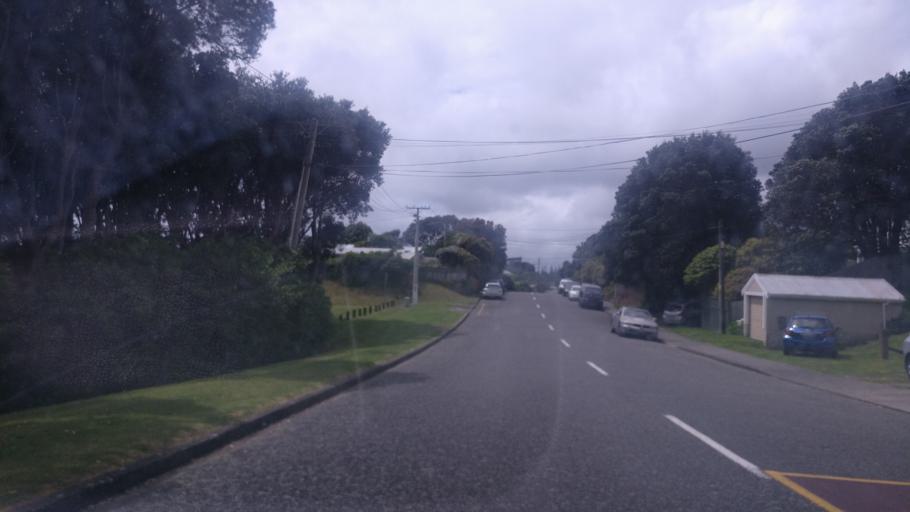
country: NZ
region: Wellington
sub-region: Kapiti Coast District
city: Paraparaumu
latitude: -40.9804
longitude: 174.9574
